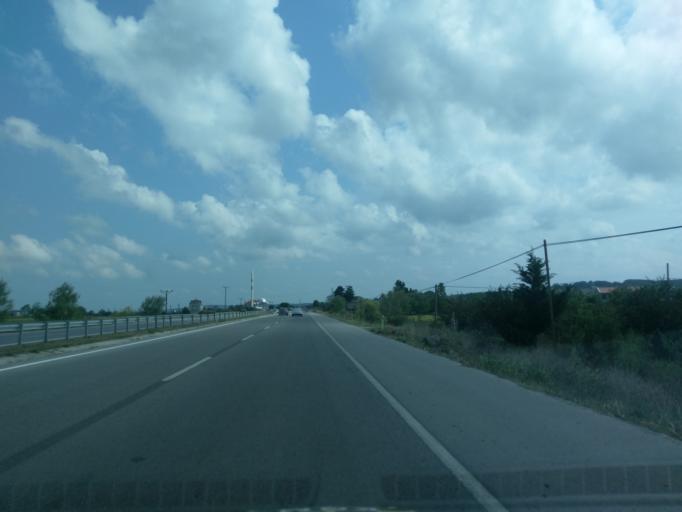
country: TR
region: Samsun
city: Bafra
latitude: 41.6016
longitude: 35.7573
